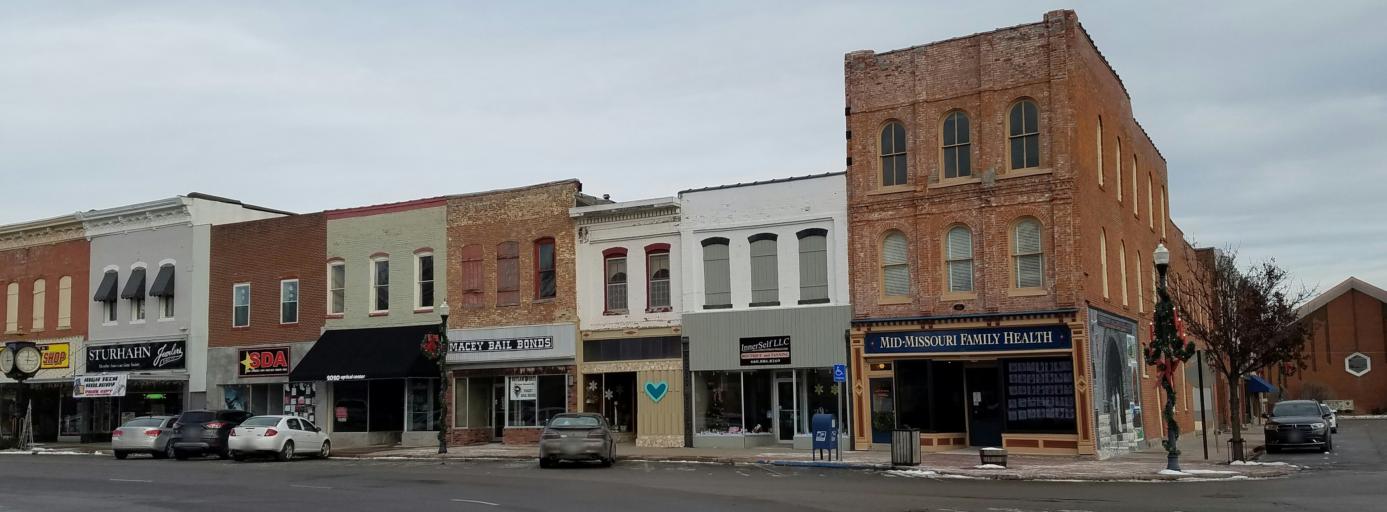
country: US
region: Missouri
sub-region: Saline County
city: Marshall
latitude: 39.1202
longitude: -93.1962
